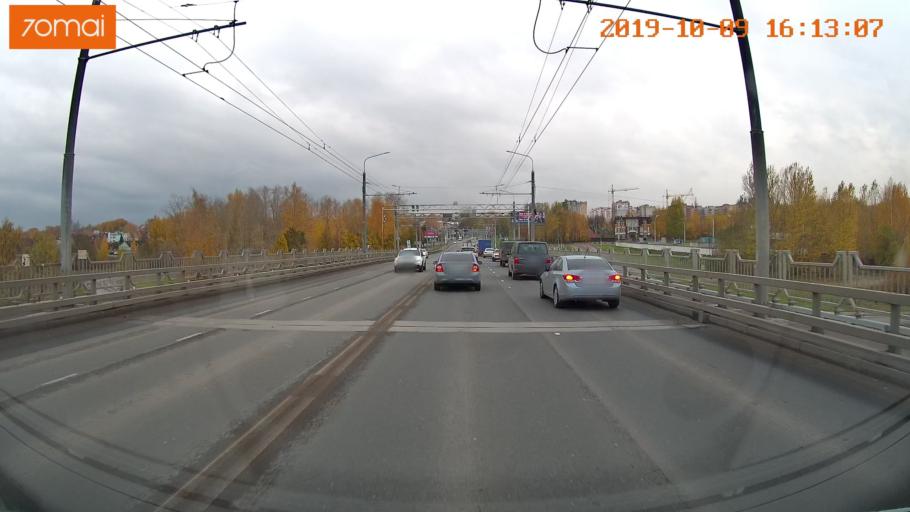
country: RU
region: Kostroma
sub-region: Kostromskoy Rayon
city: Kostroma
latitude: 57.7488
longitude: 40.9329
